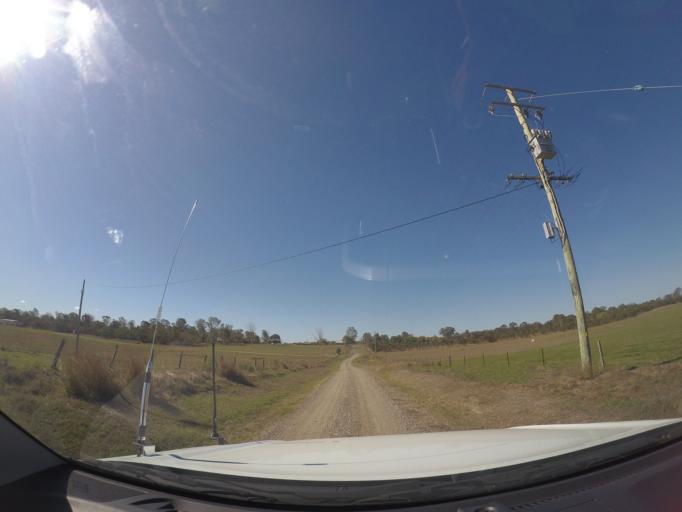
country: AU
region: Queensland
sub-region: Logan
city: North Maclean
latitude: -27.7688
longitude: 153.0467
